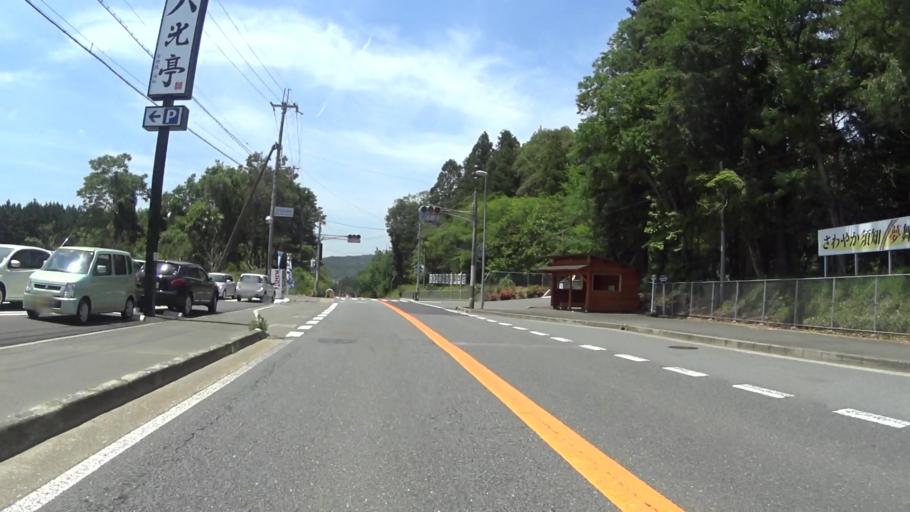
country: JP
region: Kyoto
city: Ayabe
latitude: 35.1724
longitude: 135.4138
